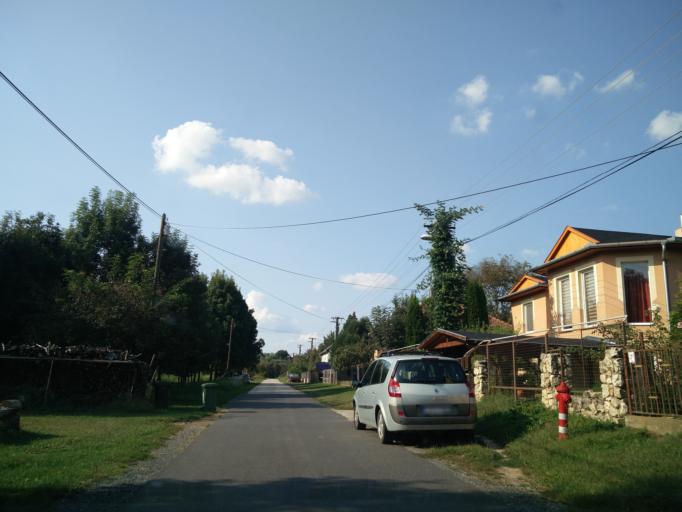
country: HU
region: Zala
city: Zalaegerszeg
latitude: 46.8678
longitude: 16.8497
